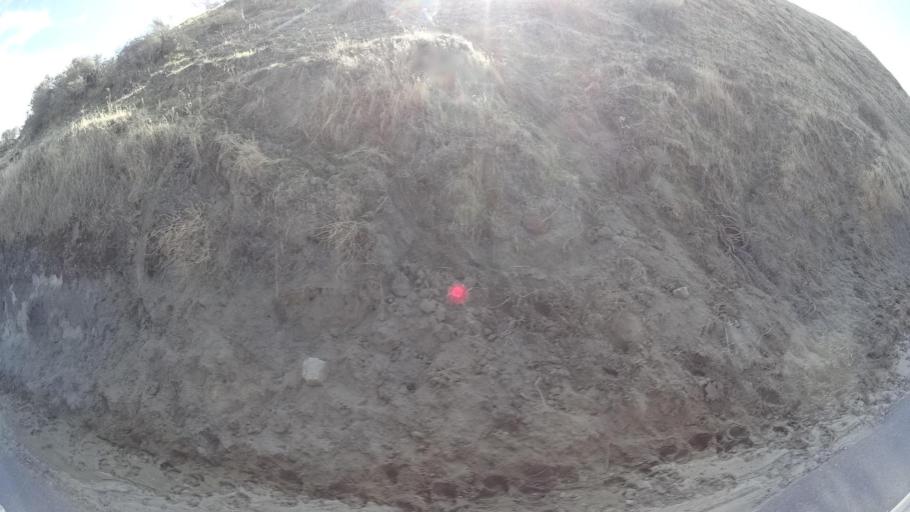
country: US
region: California
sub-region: Kern County
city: Oildale
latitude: 35.5150
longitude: -118.9007
